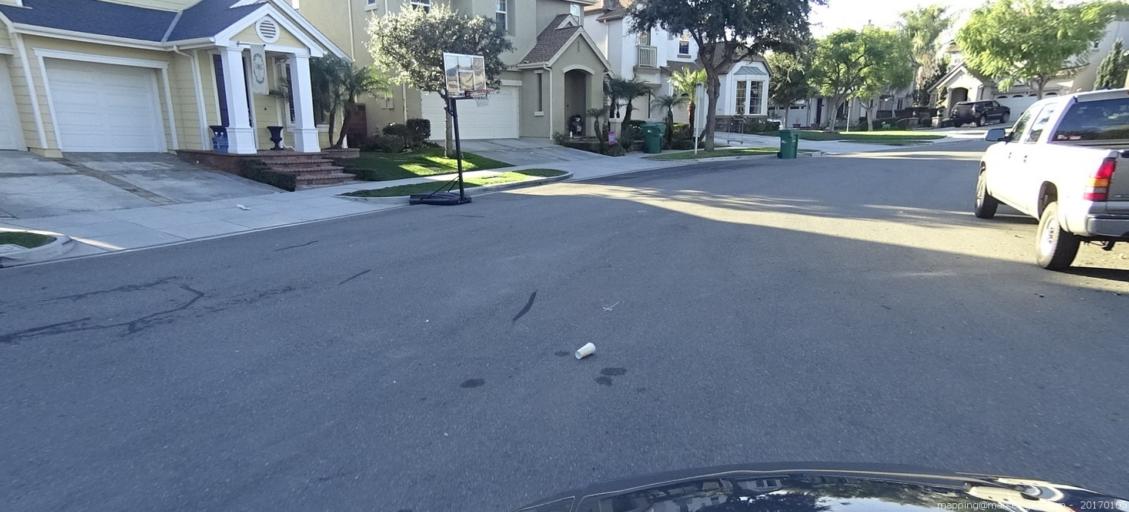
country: US
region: California
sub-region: Orange County
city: Ladera Ranch
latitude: 33.5561
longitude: -117.6398
